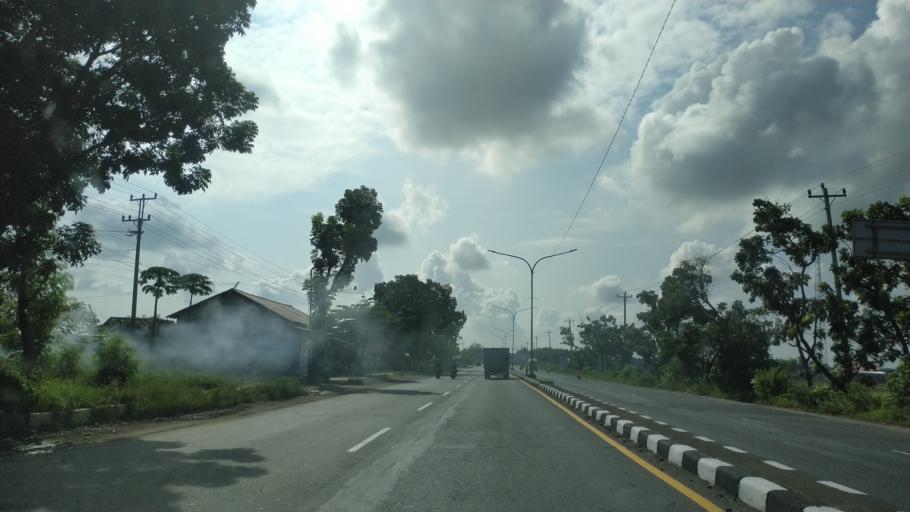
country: ID
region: Central Java
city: Comal
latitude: -6.9004
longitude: 109.5144
